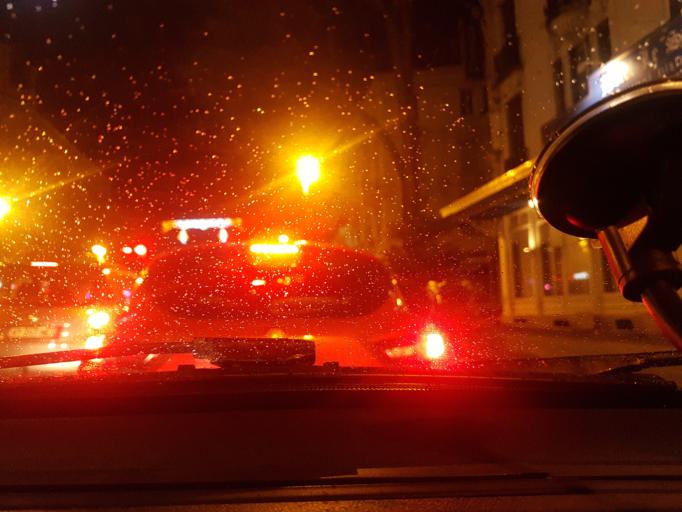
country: FR
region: Bourgogne
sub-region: Departement de Saone-et-Loire
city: Chalon-sur-Saone
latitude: 46.7838
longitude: 4.8503
